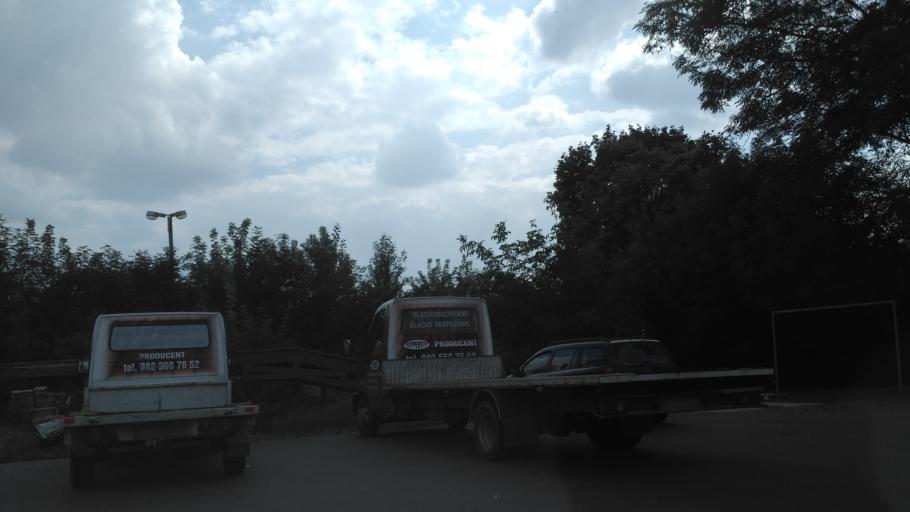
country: PL
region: Lublin Voivodeship
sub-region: Chelm
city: Chelm
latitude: 51.1421
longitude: 23.4946
